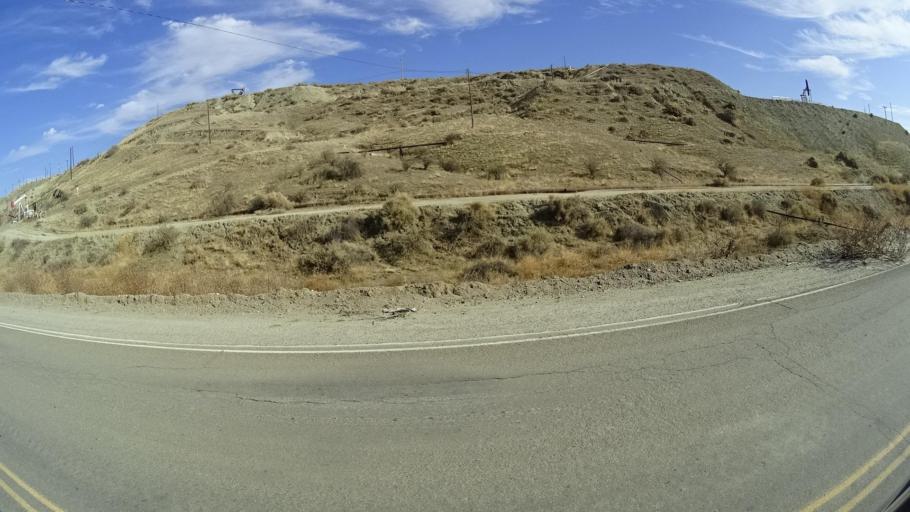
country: US
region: California
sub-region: Kern County
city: Oildale
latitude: 35.5780
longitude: -118.9597
